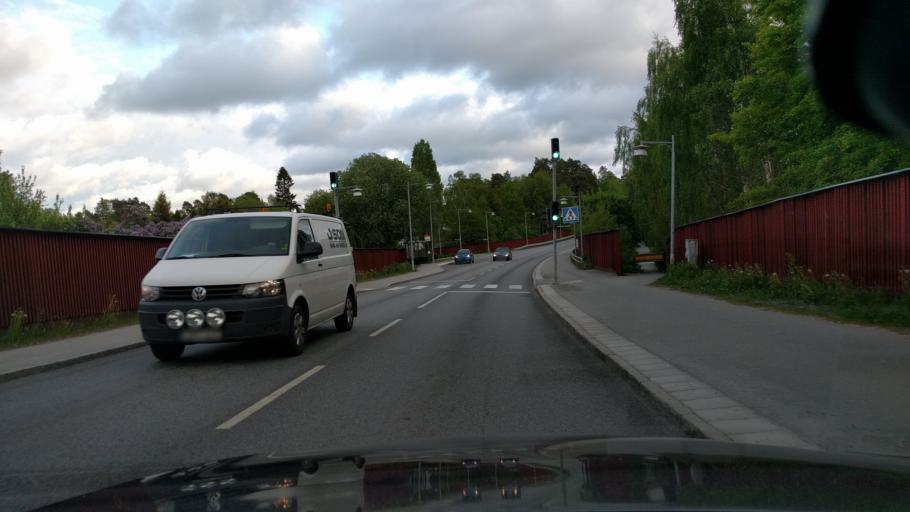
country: SE
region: Stockholm
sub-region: Vallentuna Kommun
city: Vallentuna
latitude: 59.5043
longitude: 18.0662
